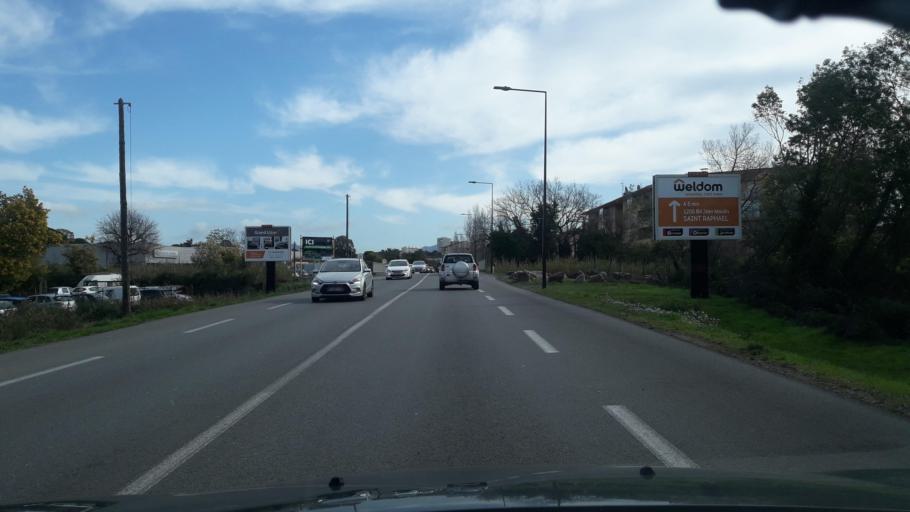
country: FR
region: Provence-Alpes-Cote d'Azur
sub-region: Departement du Var
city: Saint-Raphael
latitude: 43.4362
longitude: 6.7624
